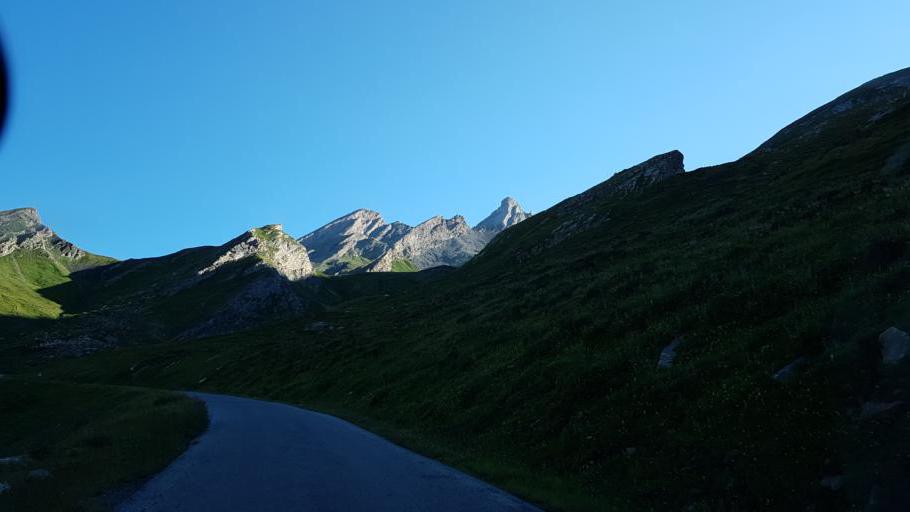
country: IT
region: Piedmont
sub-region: Provincia di Cuneo
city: Pontechianale
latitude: 44.6687
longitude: 6.9870
